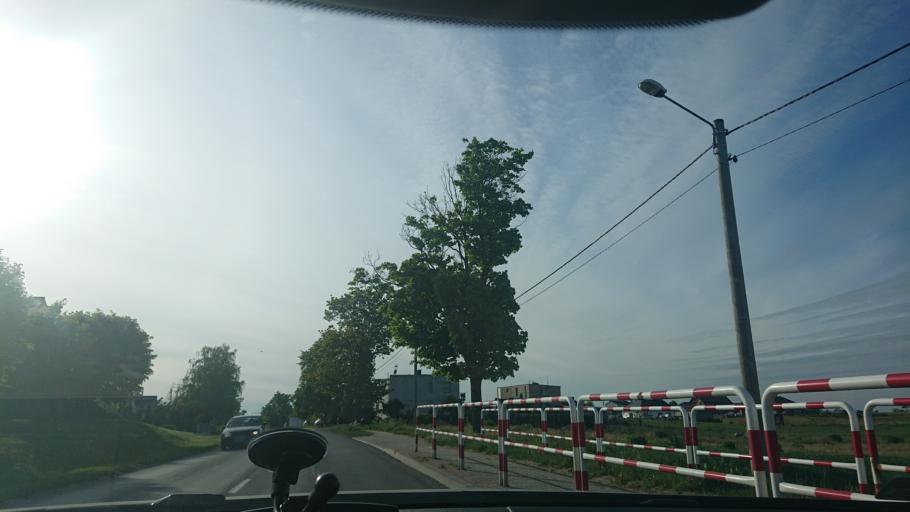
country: PL
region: Greater Poland Voivodeship
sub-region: Powiat gnieznienski
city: Gniezno
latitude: 52.5493
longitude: 17.5570
